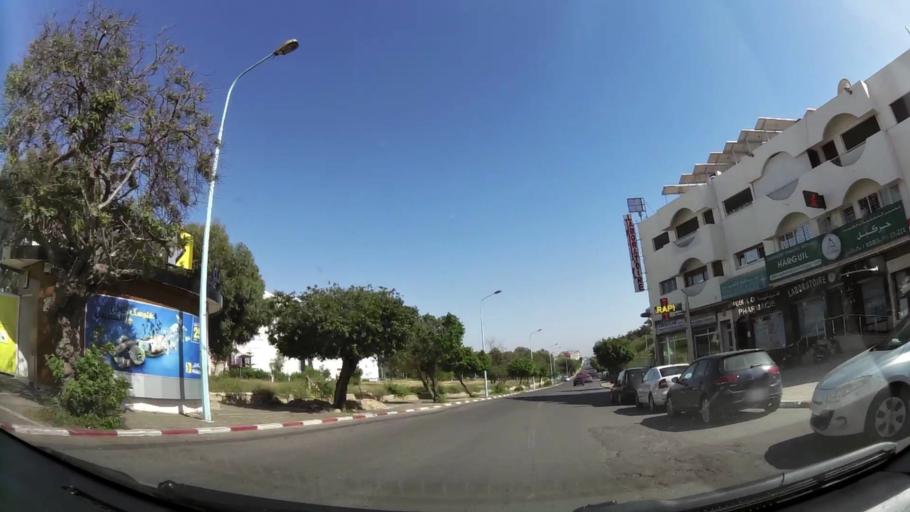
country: MA
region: Souss-Massa-Draa
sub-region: Agadir-Ida-ou-Tnan
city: Agadir
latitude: 30.4217
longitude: -9.5928
